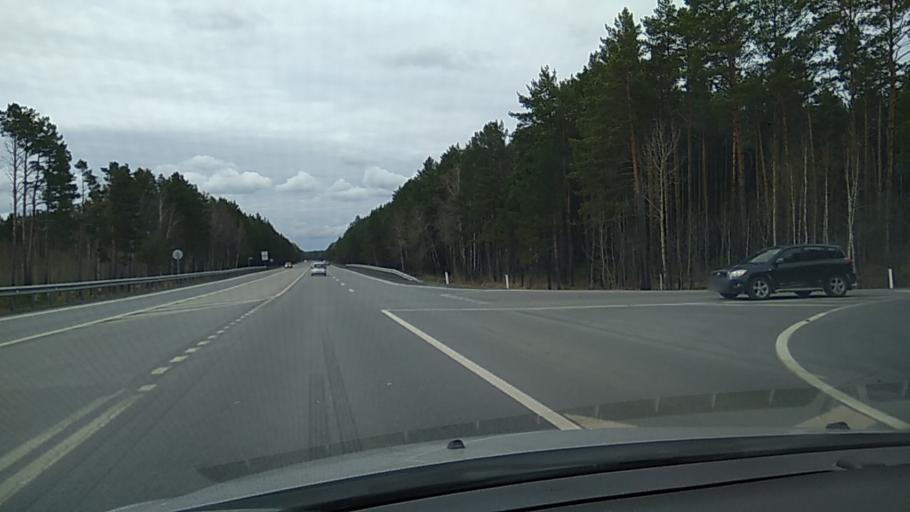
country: RU
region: Tjumen
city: Tyumen
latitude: 57.0763
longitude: 65.5161
